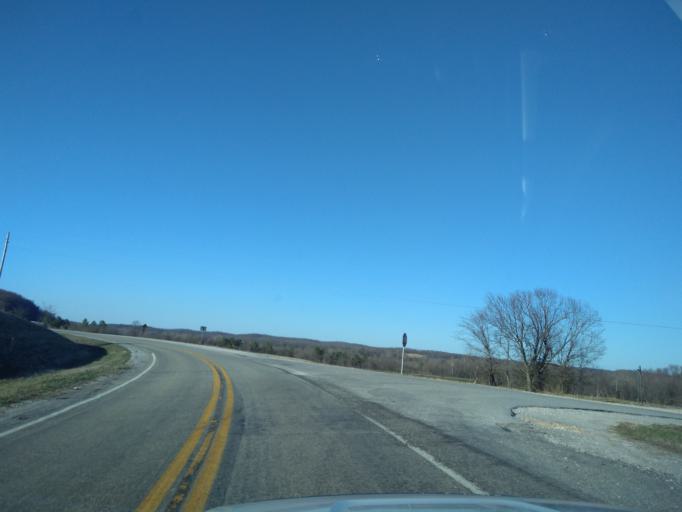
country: US
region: Arkansas
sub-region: Washington County
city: Farmington
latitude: 36.0992
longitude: -94.3488
